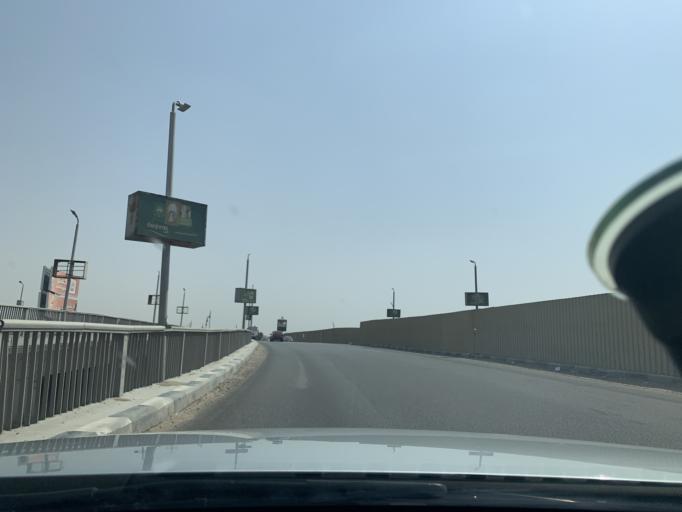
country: EG
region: Muhafazat al Qahirah
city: Cairo
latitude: 30.0816
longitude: 31.3621
